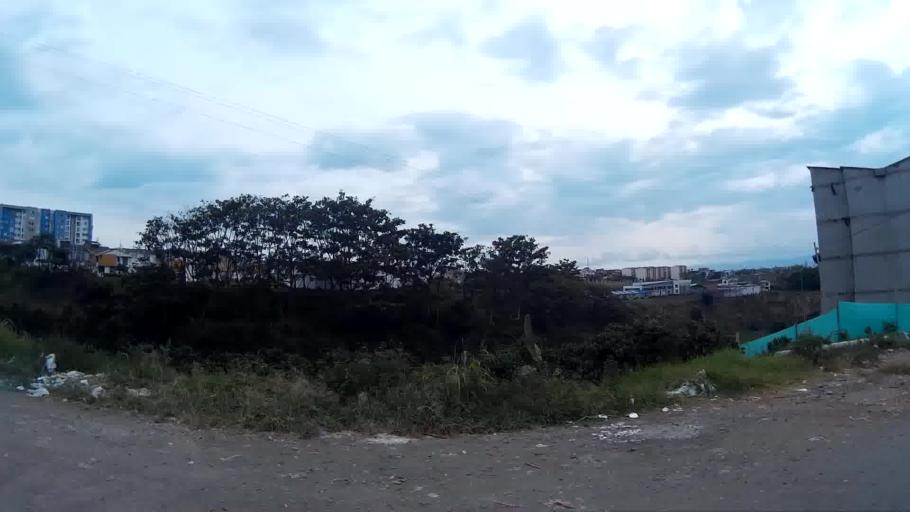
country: CO
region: Risaralda
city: Pereira
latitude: 4.7969
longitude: -75.7407
